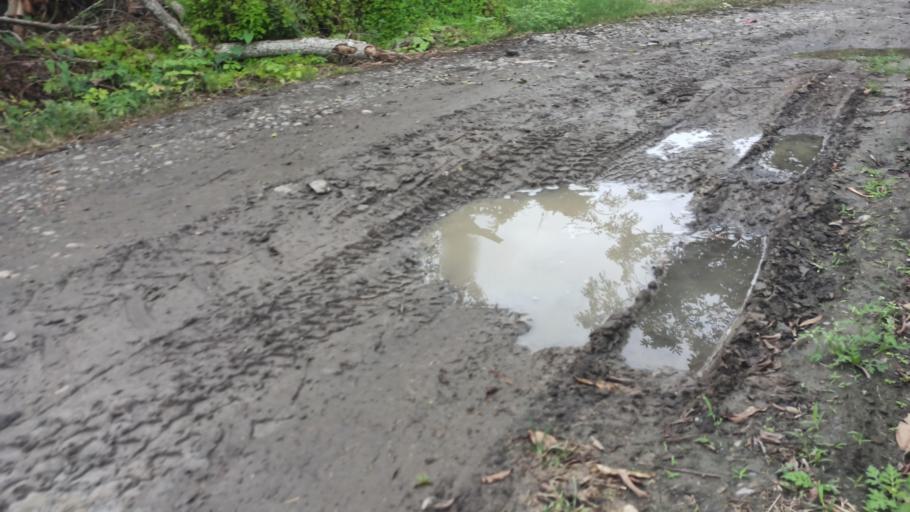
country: MX
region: Puebla
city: Espinal
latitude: 20.2985
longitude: -97.4060
